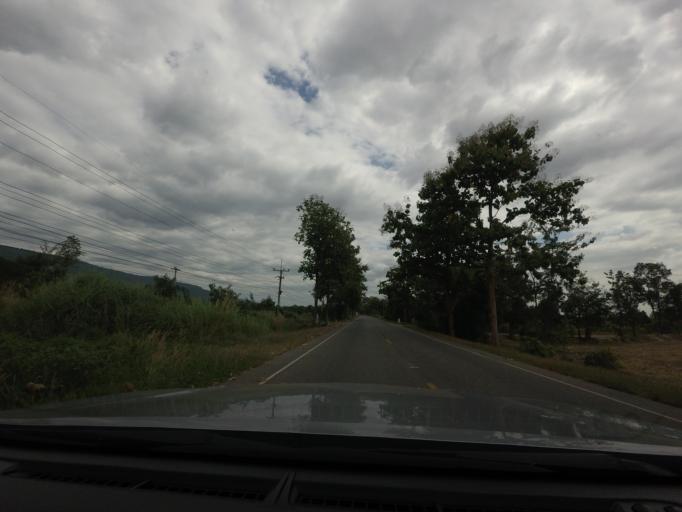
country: TH
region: Phitsanulok
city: Wang Thong
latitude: 16.7064
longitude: 100.4937
